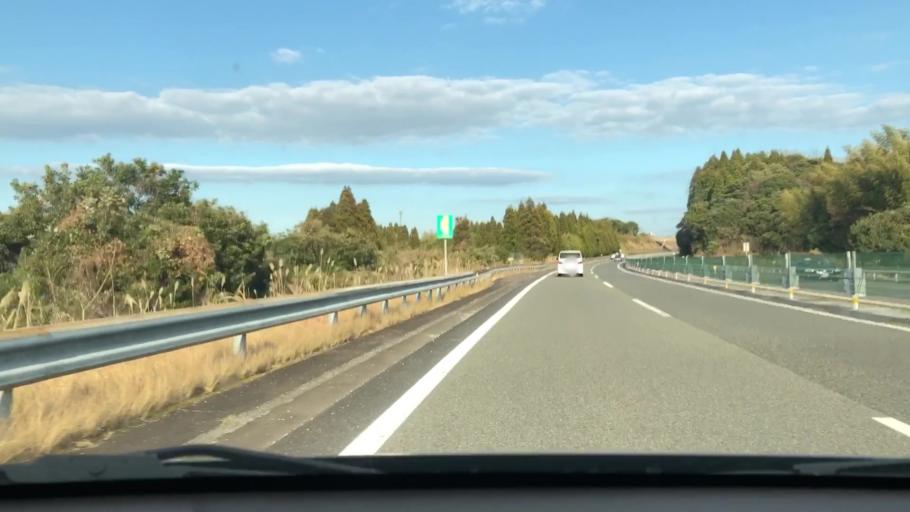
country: JP
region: Miyazaki
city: Miyazaki-shi
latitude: 31.8293
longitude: 131.3135
